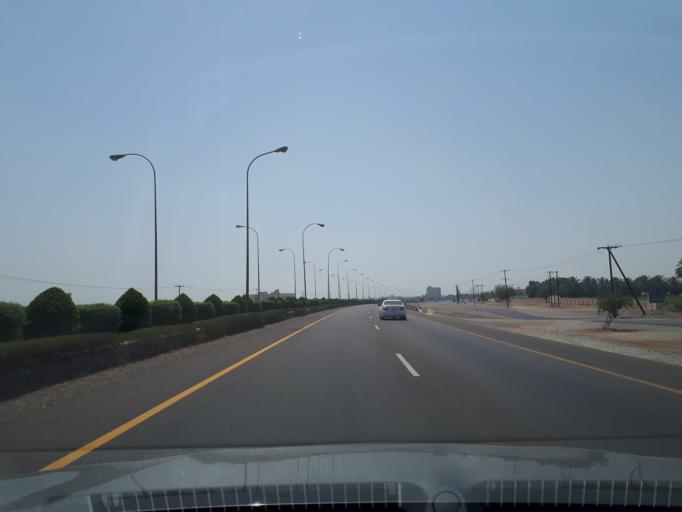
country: OM
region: Al Batinah
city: Al Sohar
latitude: 24.4117
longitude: 56.6386
